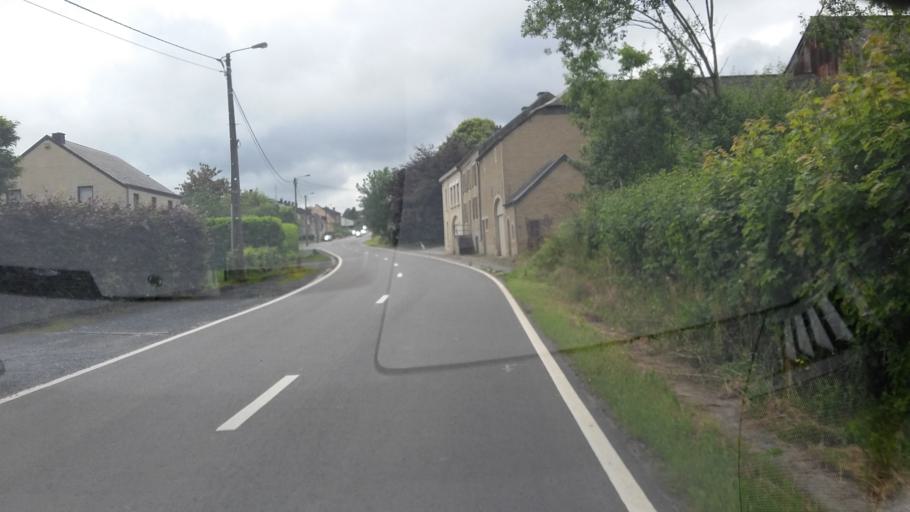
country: BE
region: Wallonia
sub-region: Province du Luxembourg
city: Arlon
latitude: 49.6921
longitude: 5.8403
